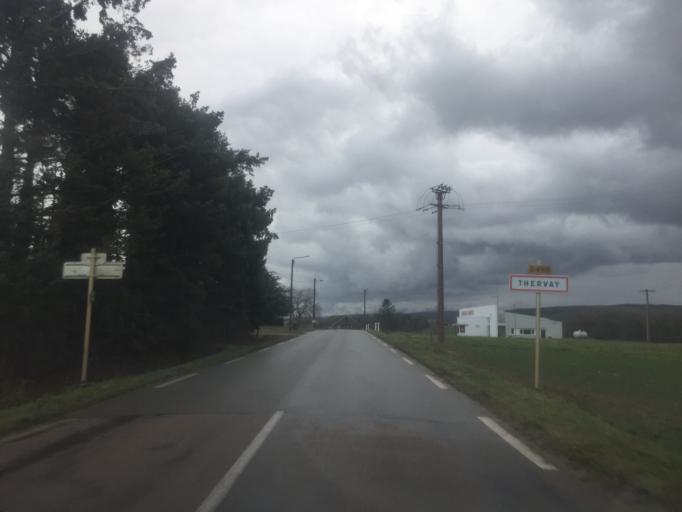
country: FR
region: Franche-Comte
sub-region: Departement de la Haute-Saone
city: Pesmes
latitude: 47.2459
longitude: 5.6064
